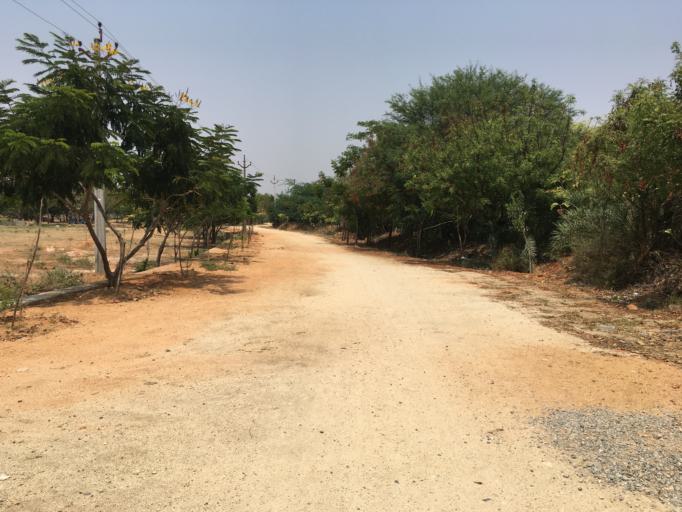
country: IN
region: Andhra Pradesh
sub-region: Anantapur
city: Puttaparthi
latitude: 14.1355
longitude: 77.7801
